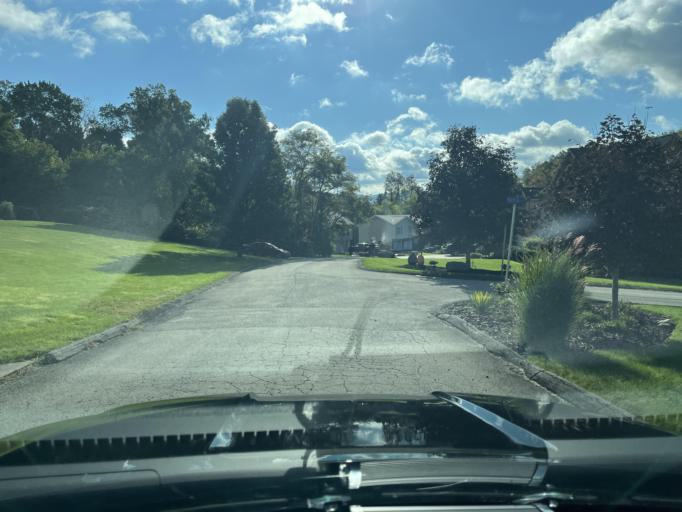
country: US
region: Pennsylvania
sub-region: Fayette County
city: South Uniontown
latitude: 39.8923
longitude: -79.7564
